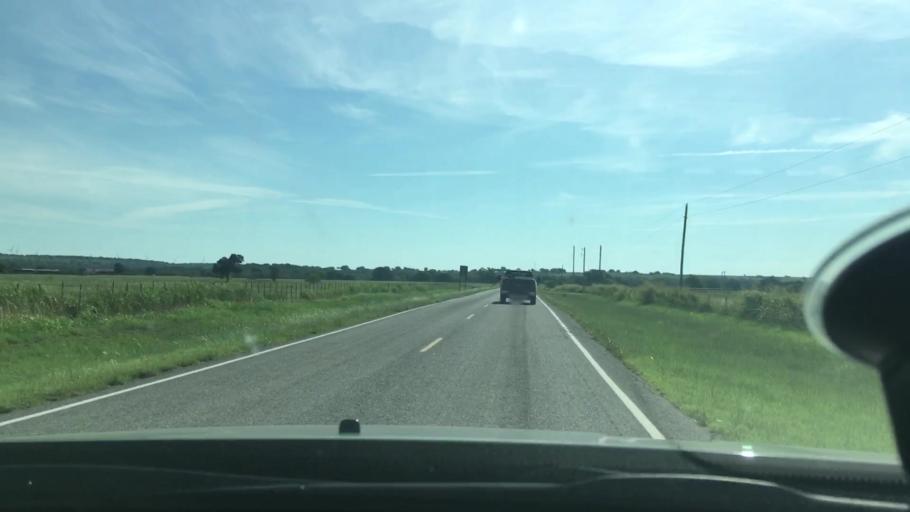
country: US
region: Oklahoma
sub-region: Carter County
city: Lone Grove
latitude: 34.3327
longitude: -97.2452
